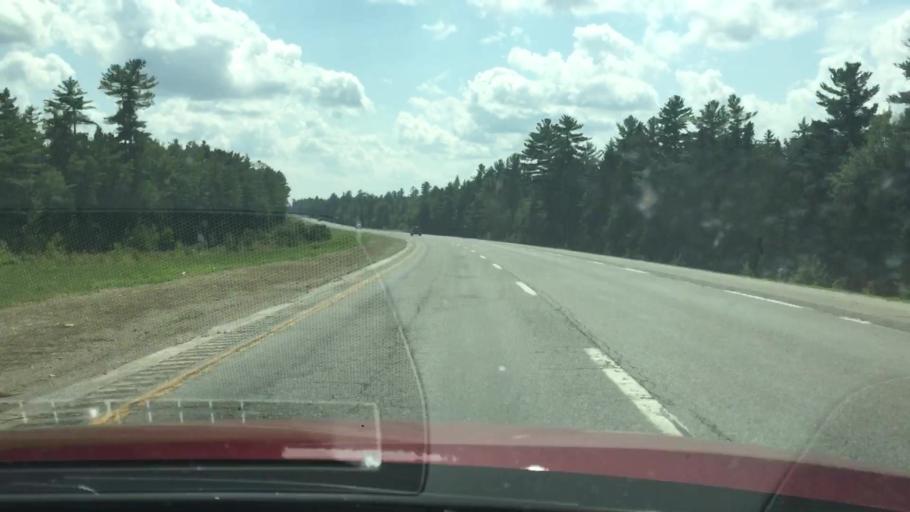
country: US
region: Maine
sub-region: Penobscot County
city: Medway
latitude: 45.5904
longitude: -68.5422
